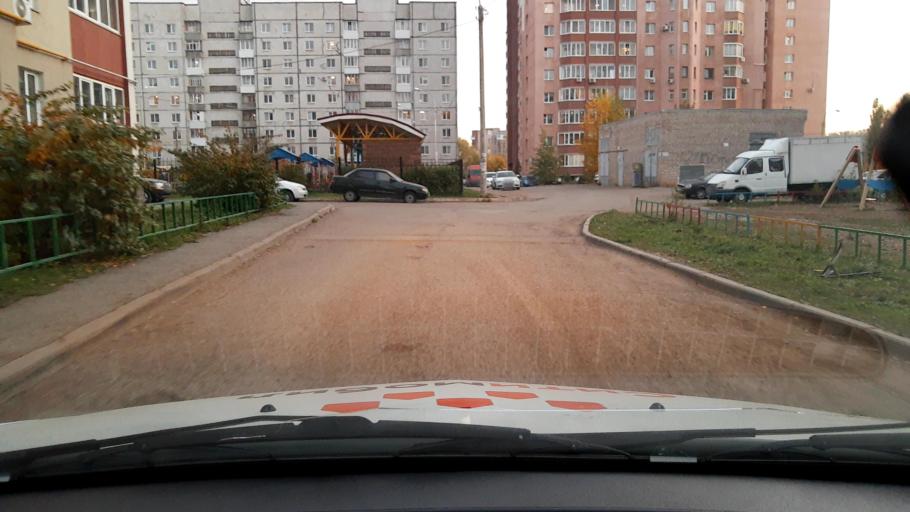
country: RU
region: Bashkortostan
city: Ufa
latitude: 54.7819
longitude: 56.1101
